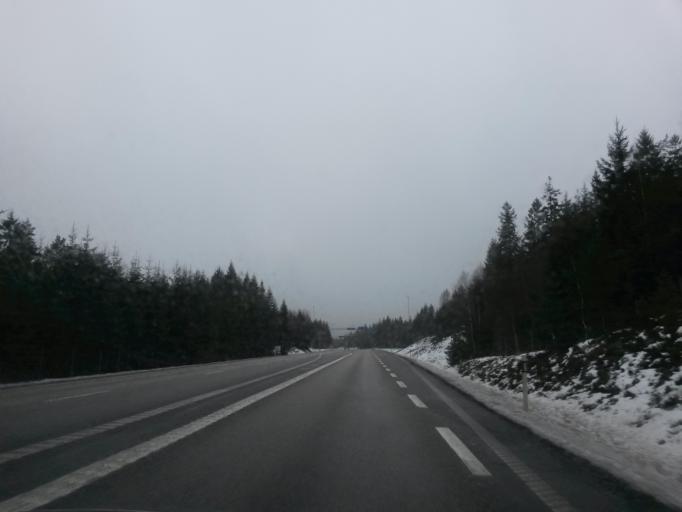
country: SE
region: Vaestra Goetaland
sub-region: Marks Kommun
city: Fritsla
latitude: 57.5404
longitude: 12.8074
